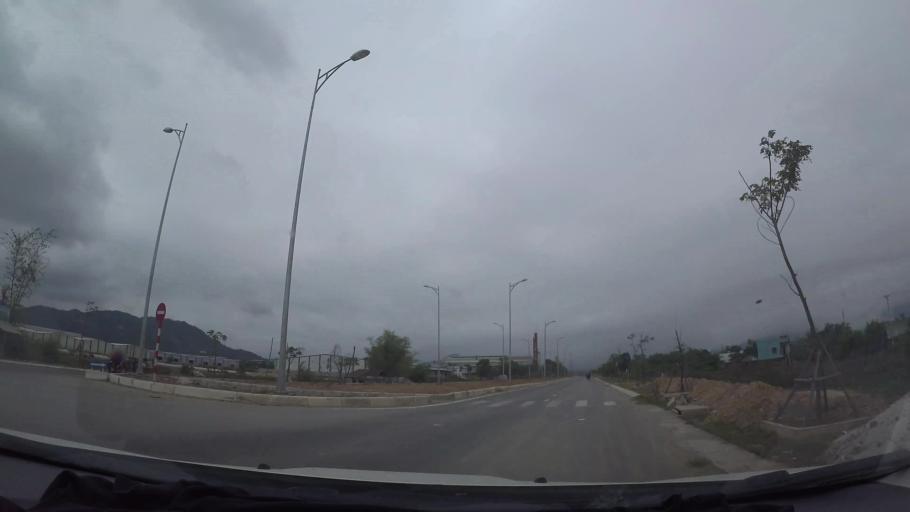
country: VN
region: Da Nang
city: Lien Chieu
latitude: 16.0908
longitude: 108.1077
